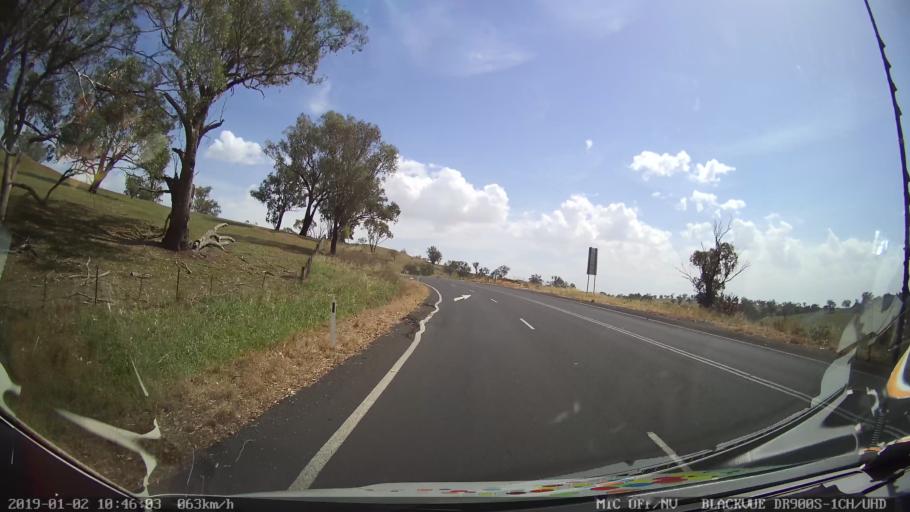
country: AU
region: New South Wales
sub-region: Cootamundra
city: Cootamundra
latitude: -34.7547
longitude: 148.2894
